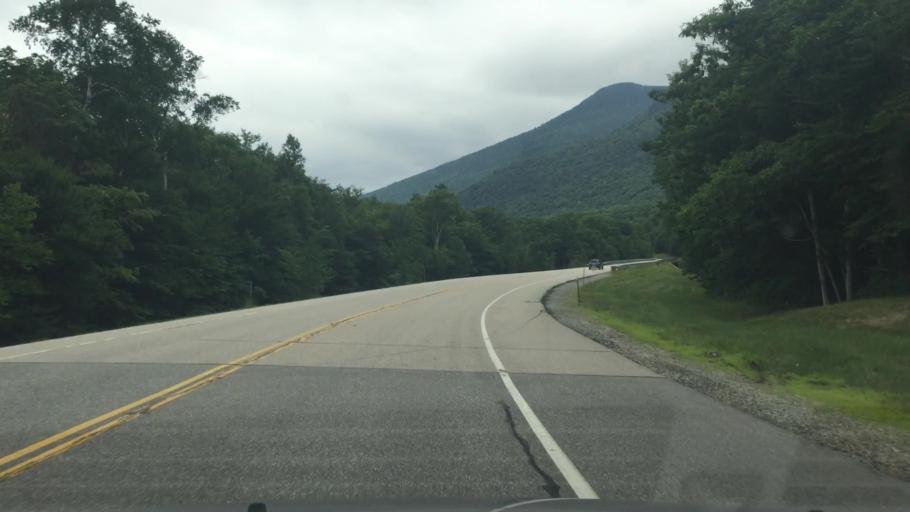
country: US
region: New Hampshire
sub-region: Carroll County
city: North Conway
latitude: 44.1550
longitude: -71.3636
